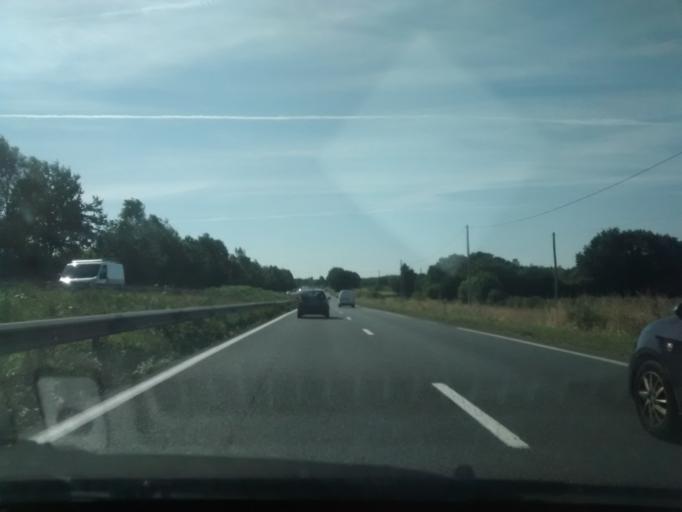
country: FR
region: Brittany
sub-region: Departement des Cotes-d'Armor
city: Plelo
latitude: 48.5299
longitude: -2.9132
